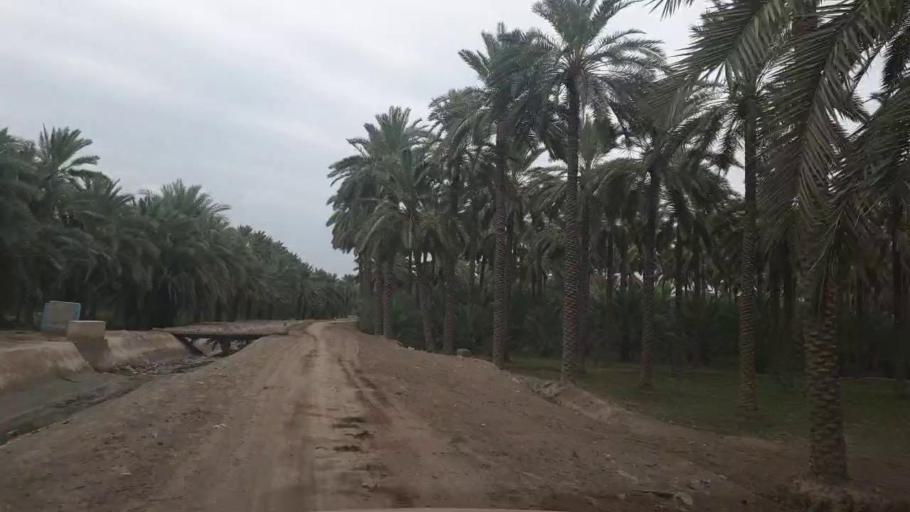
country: PK
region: Sindh
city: Khairpur
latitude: 27.6016
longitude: 68.8020
